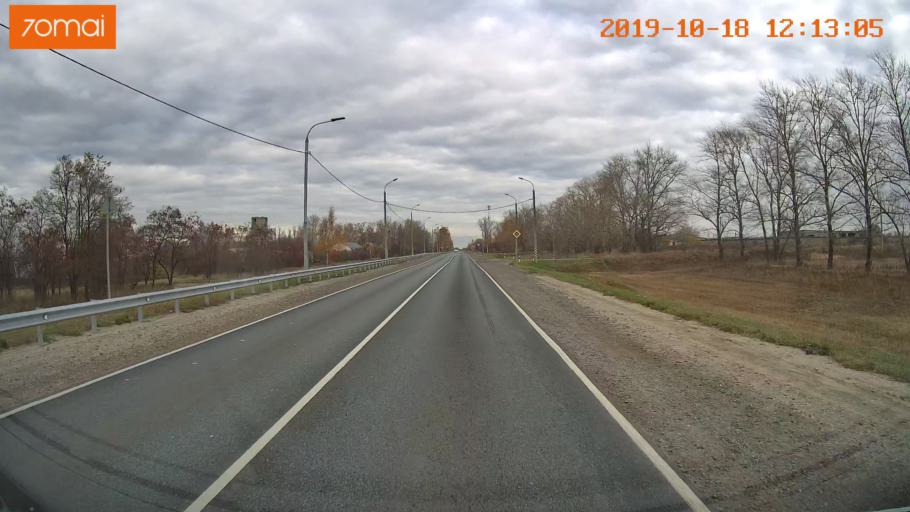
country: RU
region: Rjazan
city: Zakharovo
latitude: 54.4182
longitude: 39.3664
